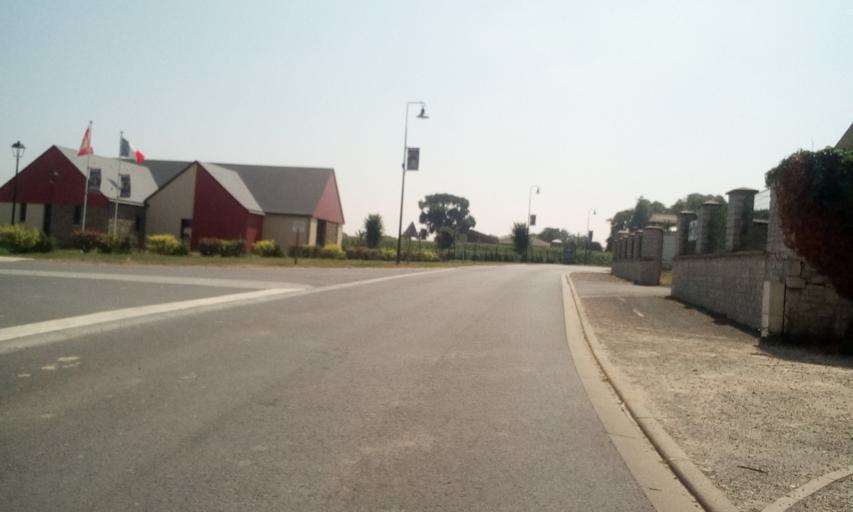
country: FR
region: Lower Normandy
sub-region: Departement du Calvados
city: Thaon
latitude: 49.2908
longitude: -0.4325
